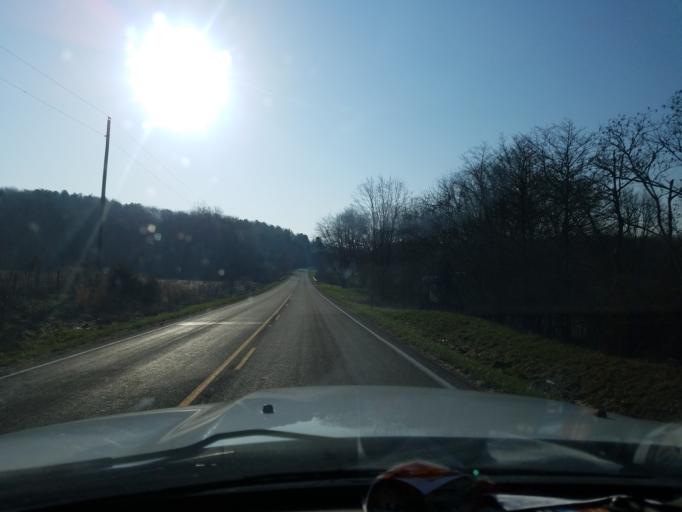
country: US
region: Indiana
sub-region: Owen County
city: Spencer
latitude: 39.3486
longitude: -86.9218
